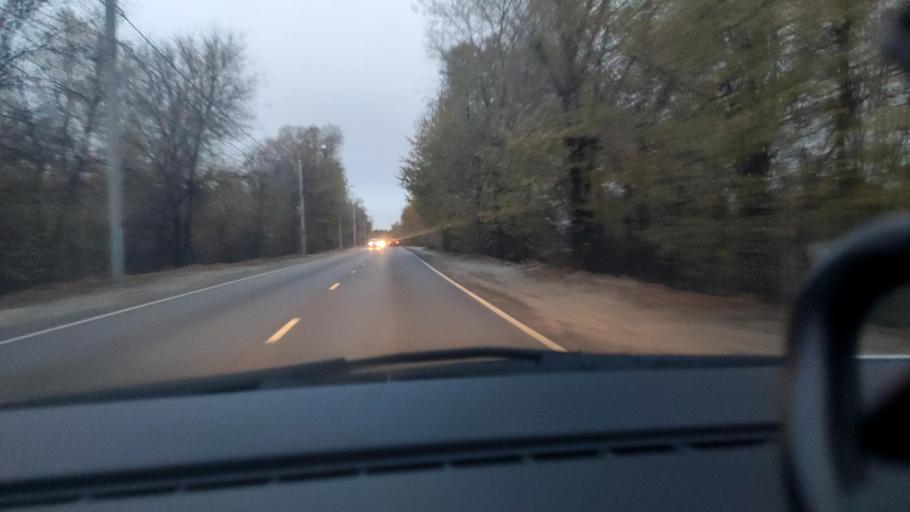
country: RU
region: Voronezj
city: Pridonskoy
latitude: 51.6409
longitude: 39.0914
